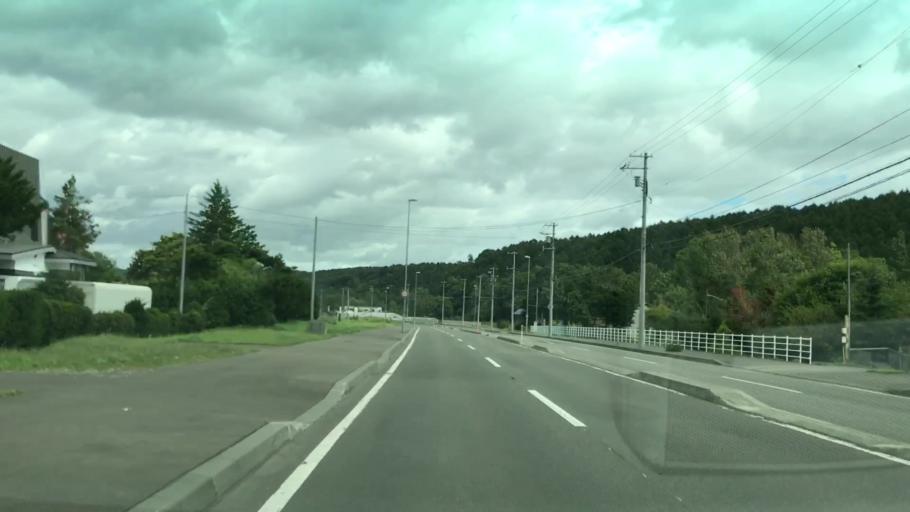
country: JP
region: Hokkaido
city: Kitahiroshima
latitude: 42.9539
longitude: 141.4523
